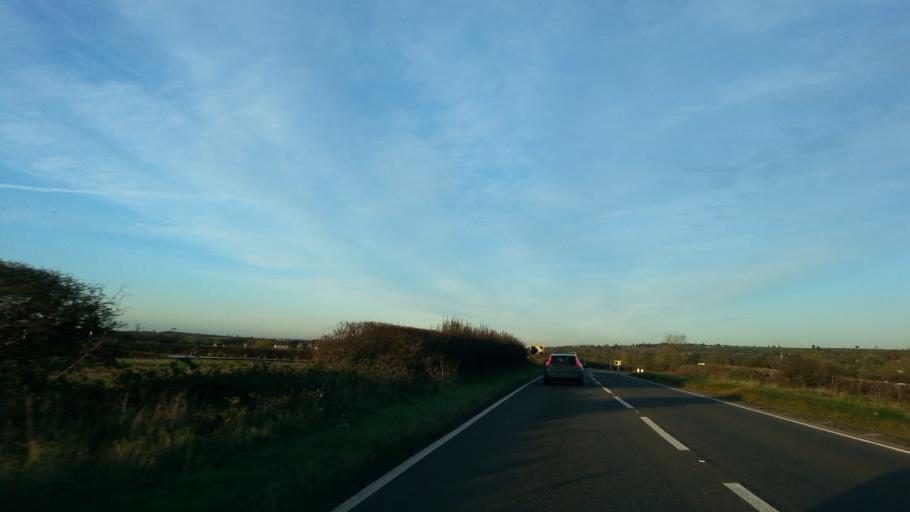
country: GB
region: England
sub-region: District of Rutland
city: Ketton
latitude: 52.5851
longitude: -0.5592
